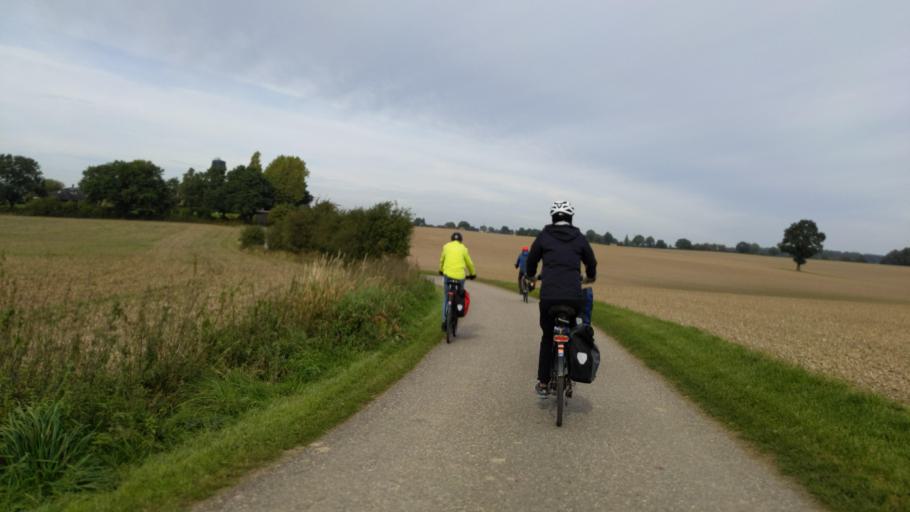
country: DE
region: Schleswig-Holstein
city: Rehhorst
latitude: 53.8830
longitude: 10.4888
